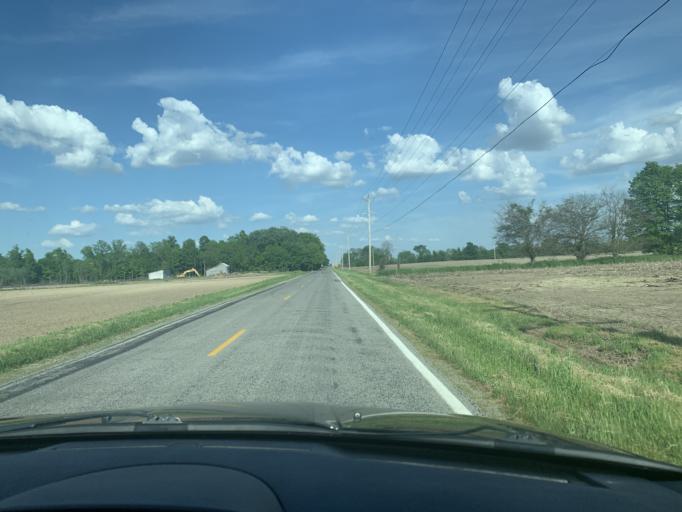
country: US
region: Ohio
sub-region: Logan County
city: De Graff
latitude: 40.2418
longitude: -83.9732
